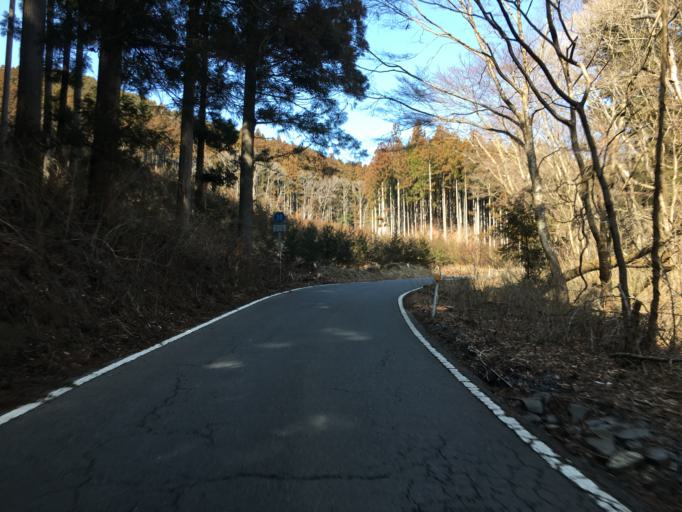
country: JP
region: Ibaraki
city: Takahagi
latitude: 36.8299
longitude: 140.5520
